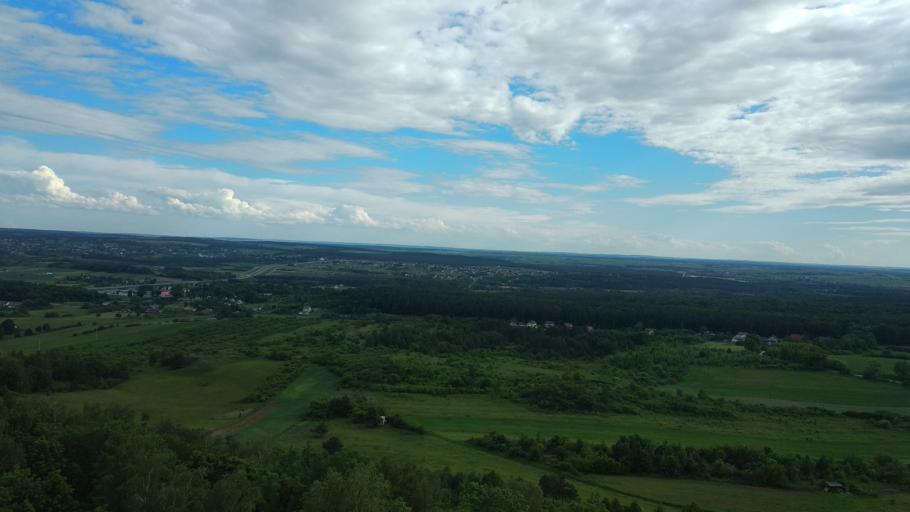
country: PL
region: Swietokrzyskie
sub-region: Powiat kielecki
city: Checiny
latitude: 50.7977
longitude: 20.4596
